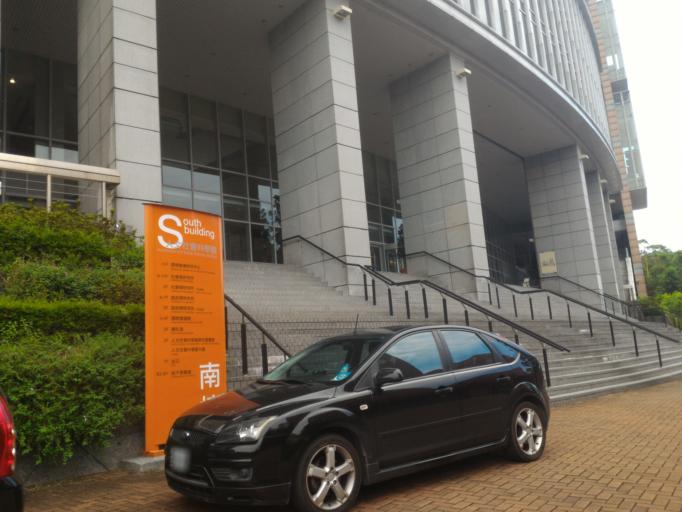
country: TW
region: Taipei
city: Taipei
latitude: 25.0410
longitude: 121.6119
